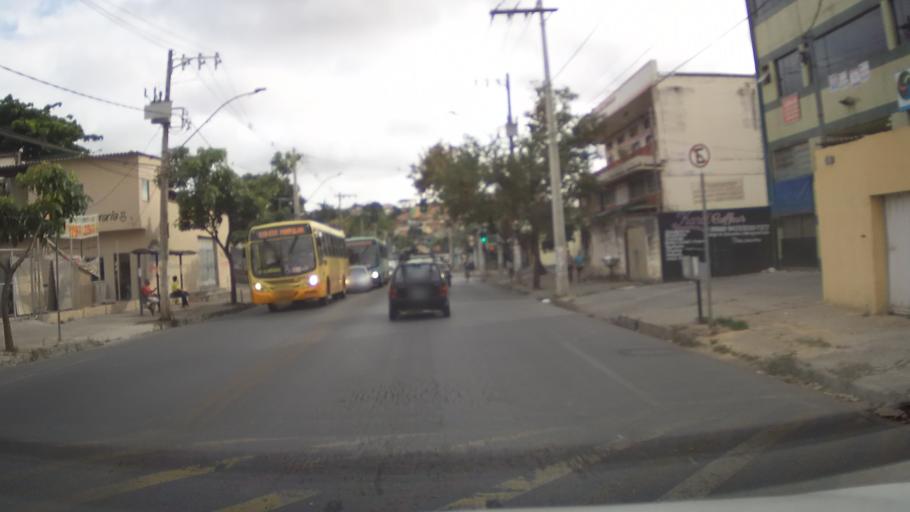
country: BR
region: Minas Gerais
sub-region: Belo Horizonte
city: Belo Horizonte
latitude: -19.8285
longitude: -43.9701
